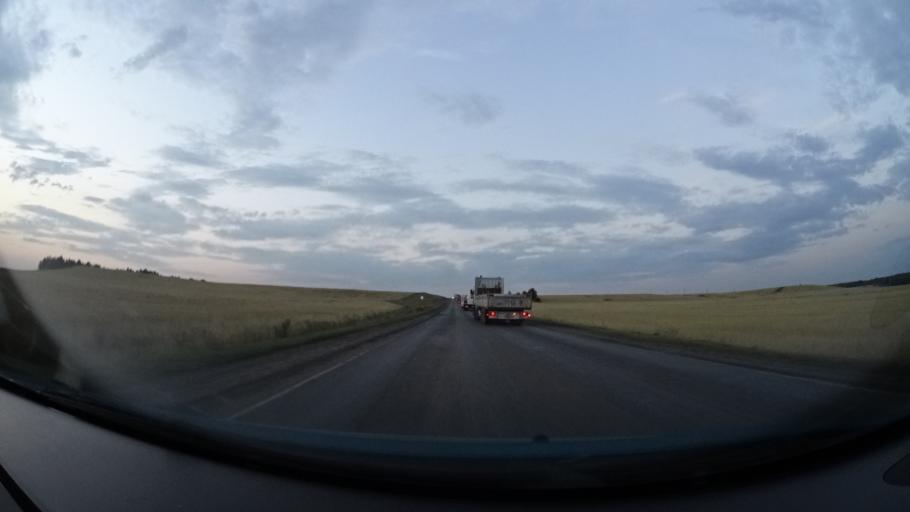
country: RU
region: Tatarstan
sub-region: Bavlinskiy Rayon
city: Bavly
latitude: 54.2926
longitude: 53.0032
